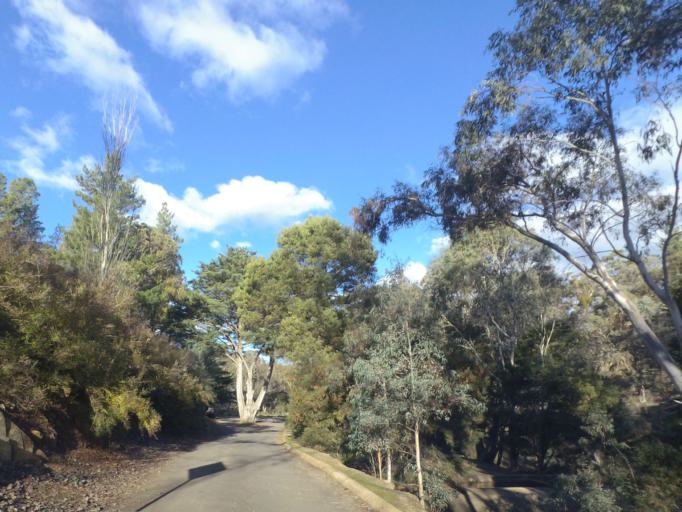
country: AU
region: Victoria
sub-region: Mount Alexander
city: Castlemaine
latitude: -37.1619
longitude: 144.2150
